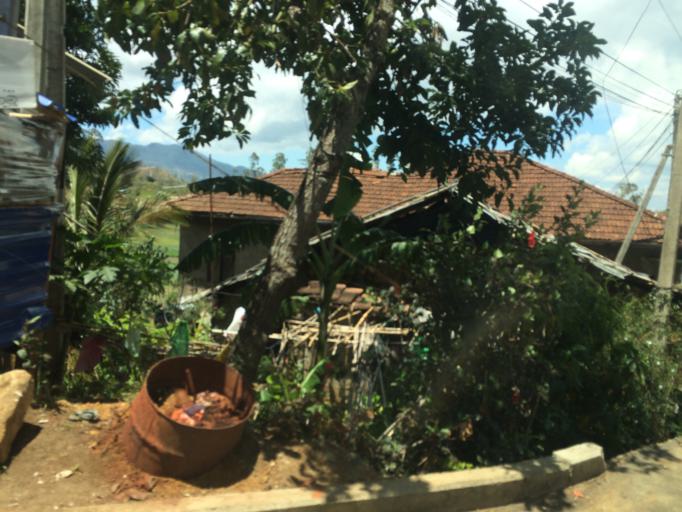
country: LK
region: Central
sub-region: Nuwara Eliya District
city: Nuwara Eliya
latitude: 6.9047
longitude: 80.8458
